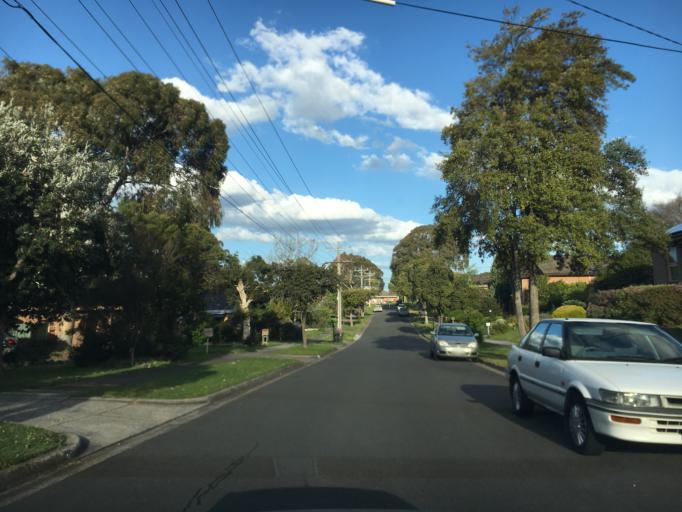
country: AU
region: Victoria
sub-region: Whitehorse
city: Vermont South
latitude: -37.8815
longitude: 145.1758
